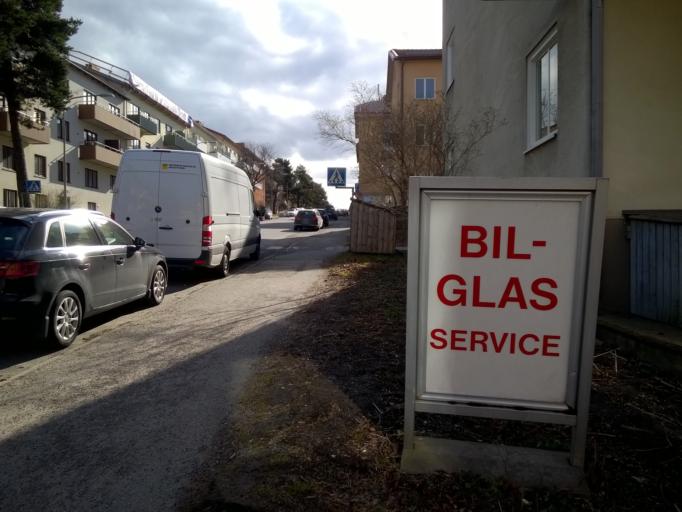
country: SE
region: Stockholm
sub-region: Sundbybergs Kommun
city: Sundbyberg
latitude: 59.3346
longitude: 17.9798
